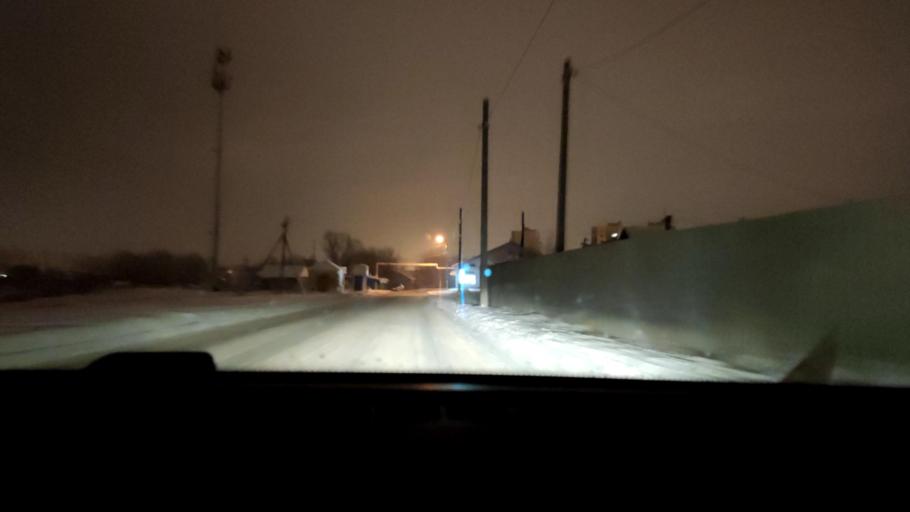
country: RU
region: Samara
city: Samara
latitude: 53.1531
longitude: 50.0881
